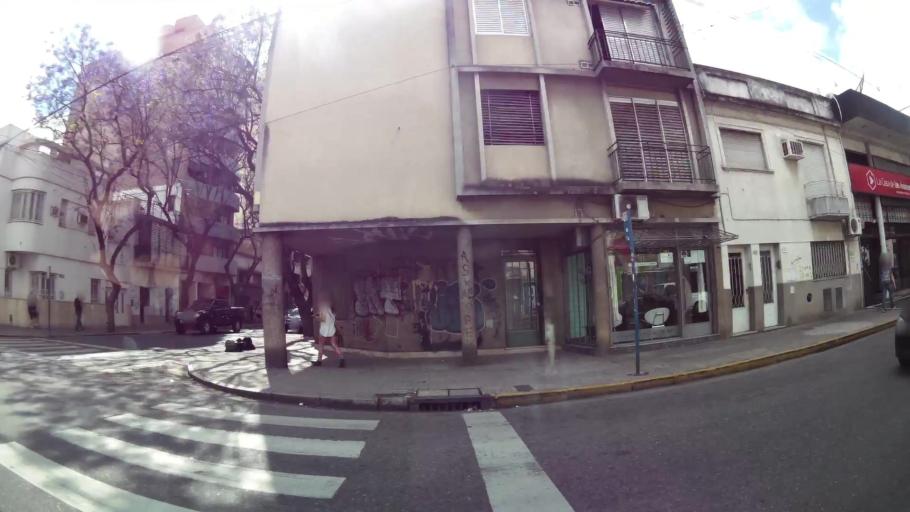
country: AR
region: Santa Fe
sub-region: Departamento de Rosario
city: Rosario
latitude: -32.9516
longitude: -60.6468
